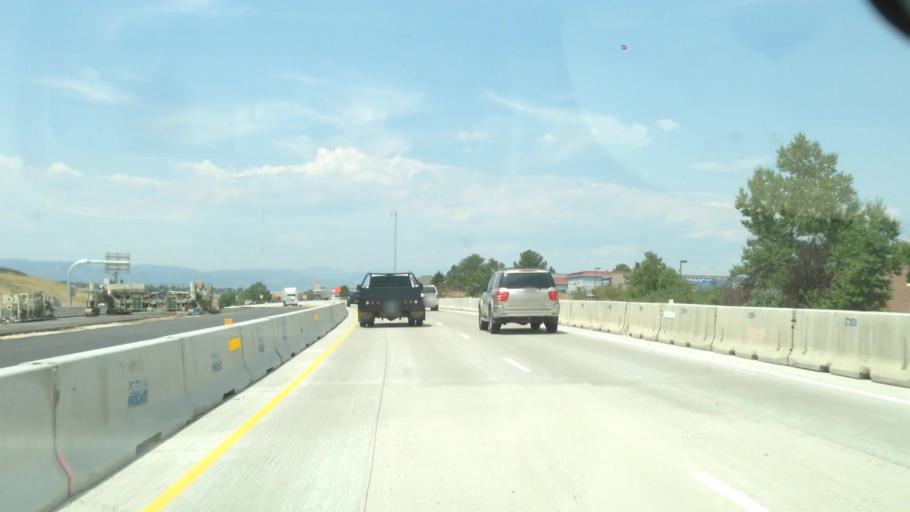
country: US
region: Colorado
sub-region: Douglas County
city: Acres Green
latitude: 39.5650
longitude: -104.9161
